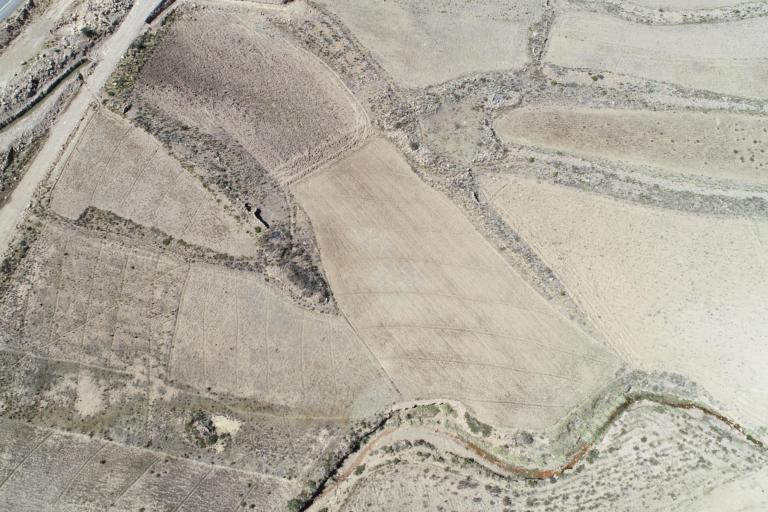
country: BO
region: La Paz
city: Achacachi
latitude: -15.8881
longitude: -68.8108
